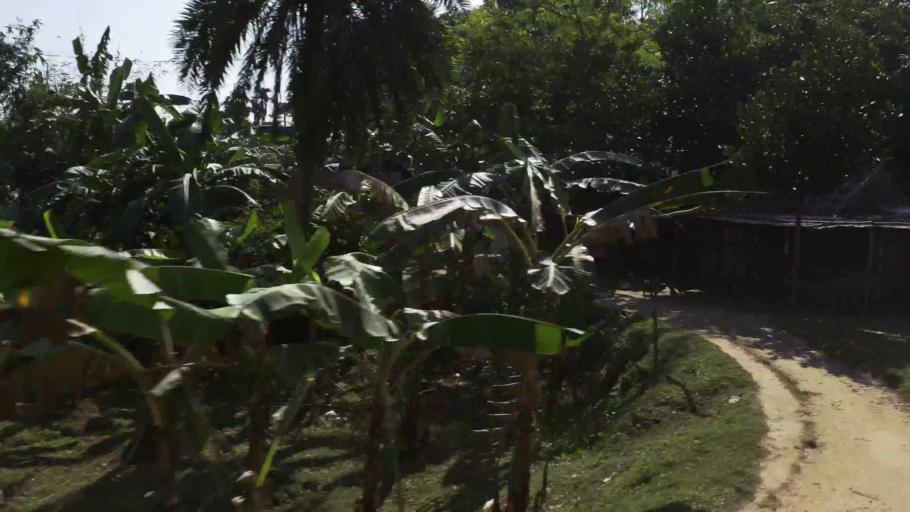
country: BD
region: Dhaka
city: Gafargaon
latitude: 24.5604
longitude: 90.5084
